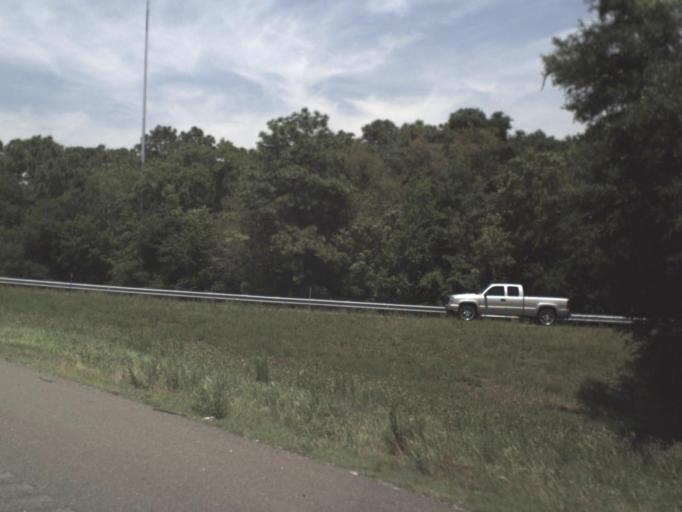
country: US
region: Florida
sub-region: Duval County
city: Jacksonville
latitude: 30.4327
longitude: -81.5788
